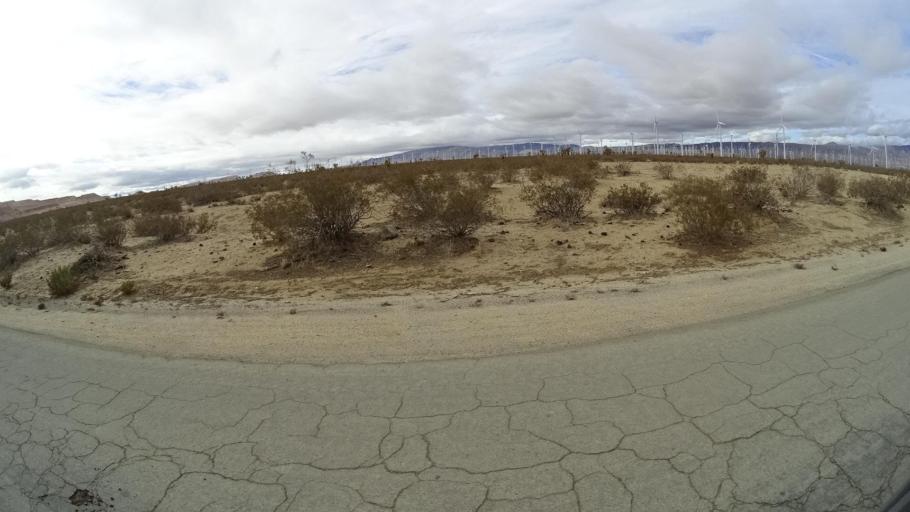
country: US
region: California
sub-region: Kern County
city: Mojave
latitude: 35.0074
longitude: -118.1857
